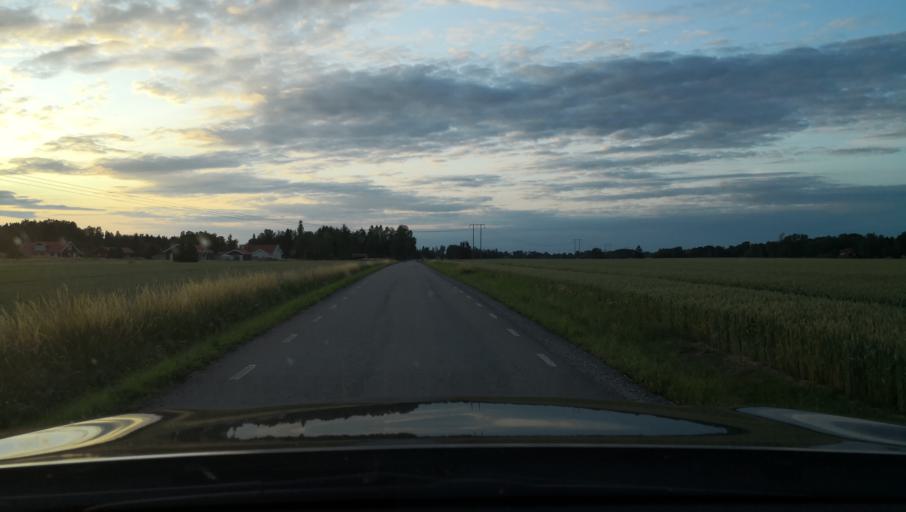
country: SE
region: Uppsala
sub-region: Uppsala Kommun
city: Storvreta
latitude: 60.0209
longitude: 17.6664
